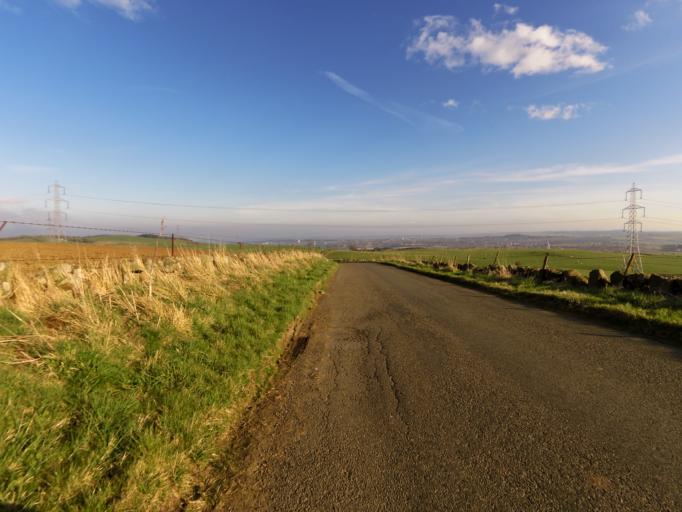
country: GB
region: Scotland
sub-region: Fife
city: Leslie
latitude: 56.2241
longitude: -3.2221
